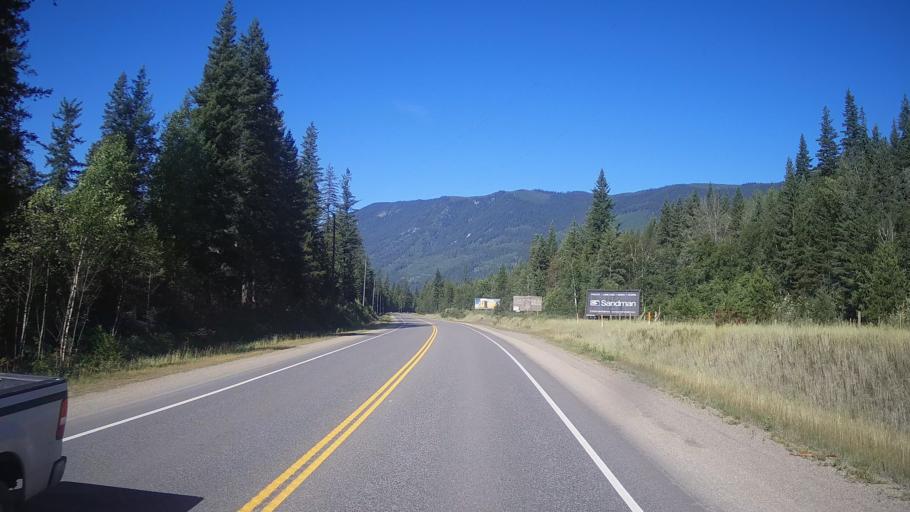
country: CA
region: British Columbia
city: Chase
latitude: 51.6726
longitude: -119.6176
